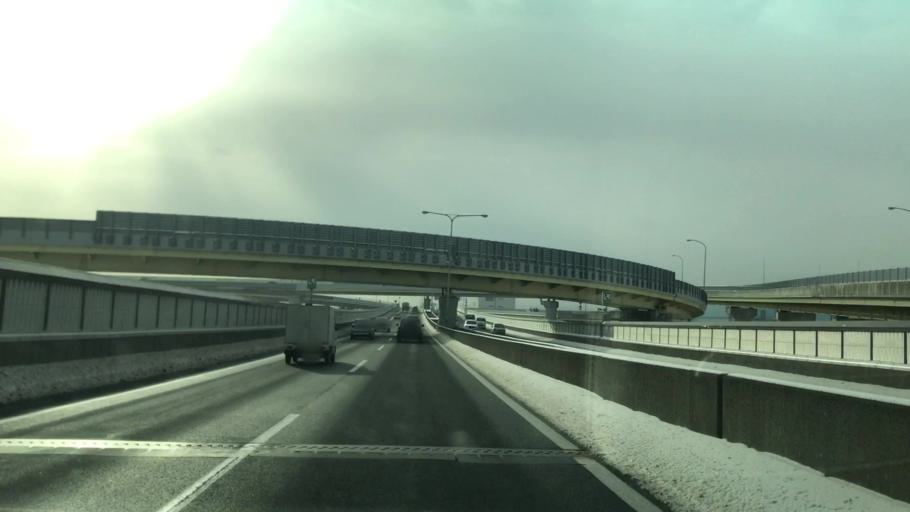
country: JP
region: Hokkaido
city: Sapporo
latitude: 43.0785
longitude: 141.4202
